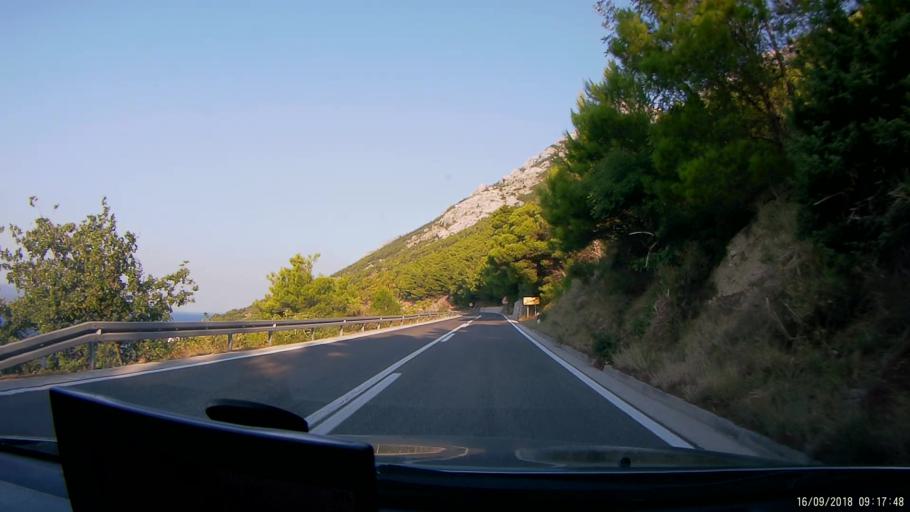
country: HR
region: Splitsko-Dalmatinska
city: Donja Brela
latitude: 43.4029
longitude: 16.8516
